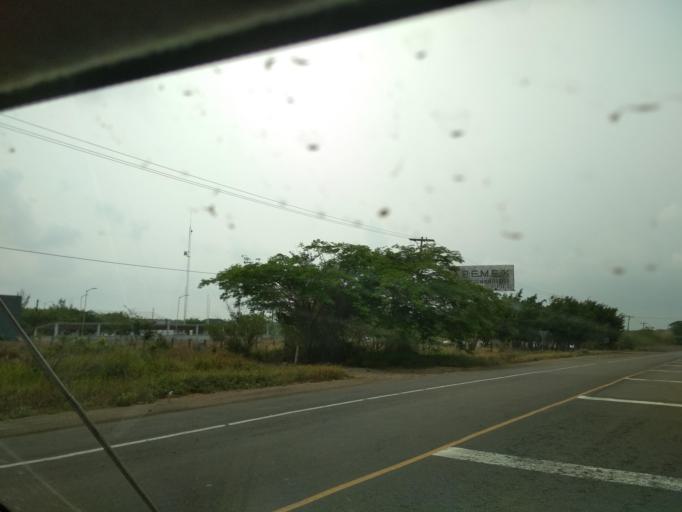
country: MX
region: Veracruz
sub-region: Medellin
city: La Laguna y Monte del Castillo
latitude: 19.0003
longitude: -96.1054
